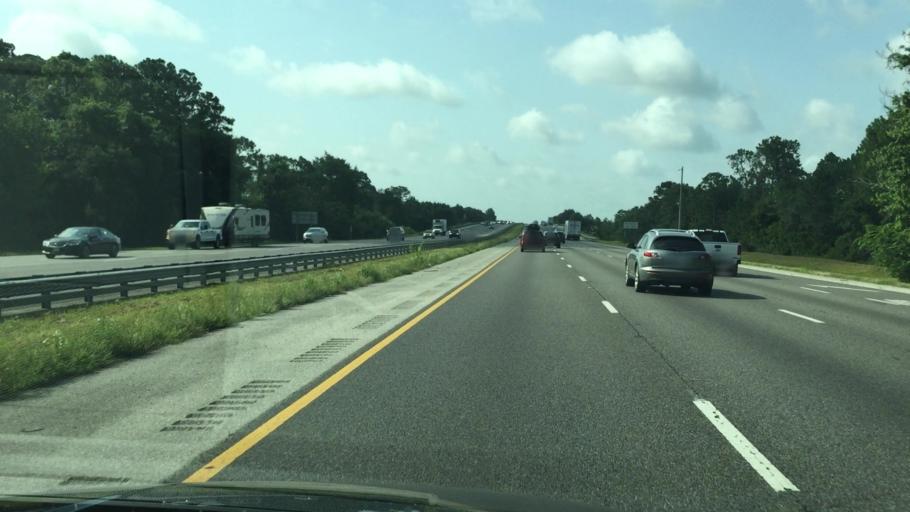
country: US
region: Florida
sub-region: Flagler County
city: Flagler Beach
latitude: 29.5020
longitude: -81.1939
